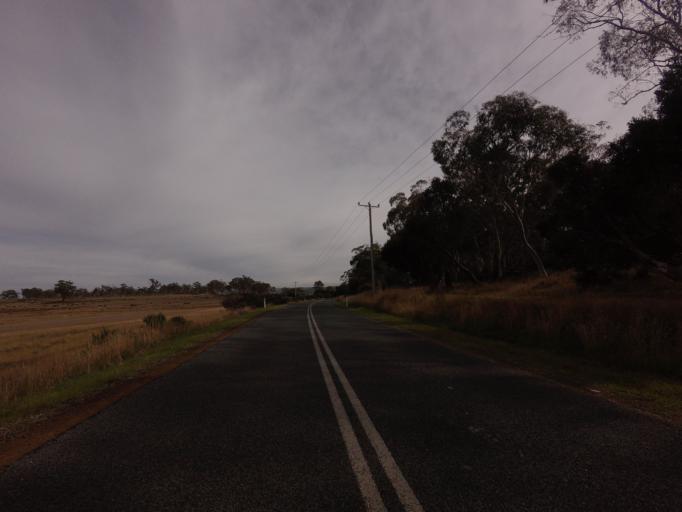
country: AU
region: Tasmania
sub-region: Brighton
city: Bridgewater
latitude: -42.3313
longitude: 147.3960
